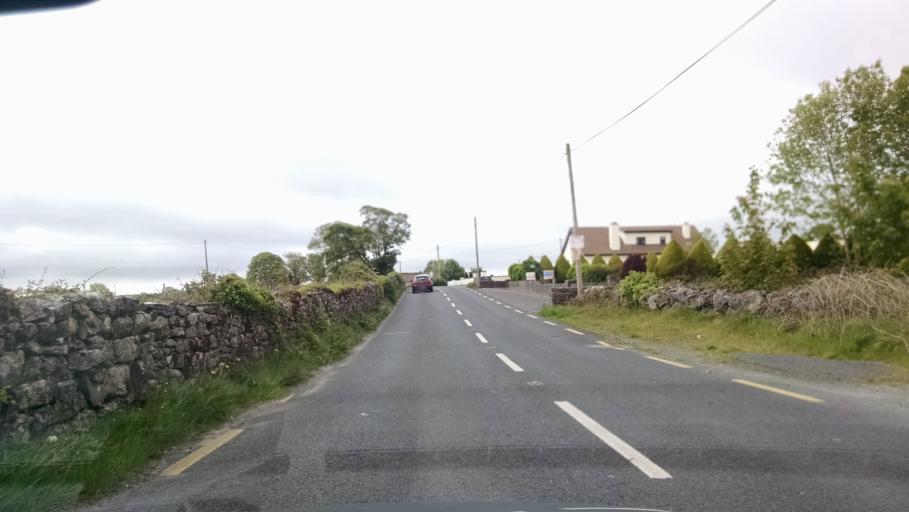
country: IE
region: Connaught
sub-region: County Galway
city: Moycullen
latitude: 53.4776
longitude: -9.0928
